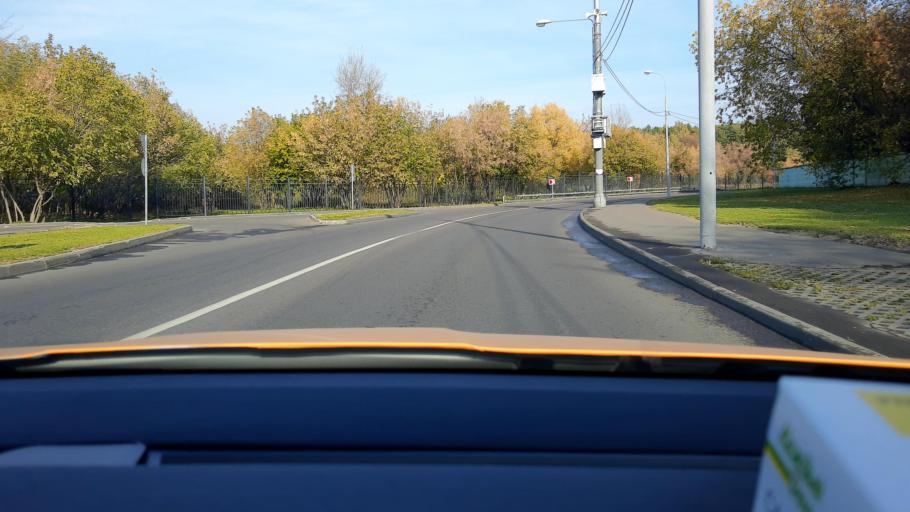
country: RU
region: Moscow
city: Kuz'minki
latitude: 55.6826
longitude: 37.7815
